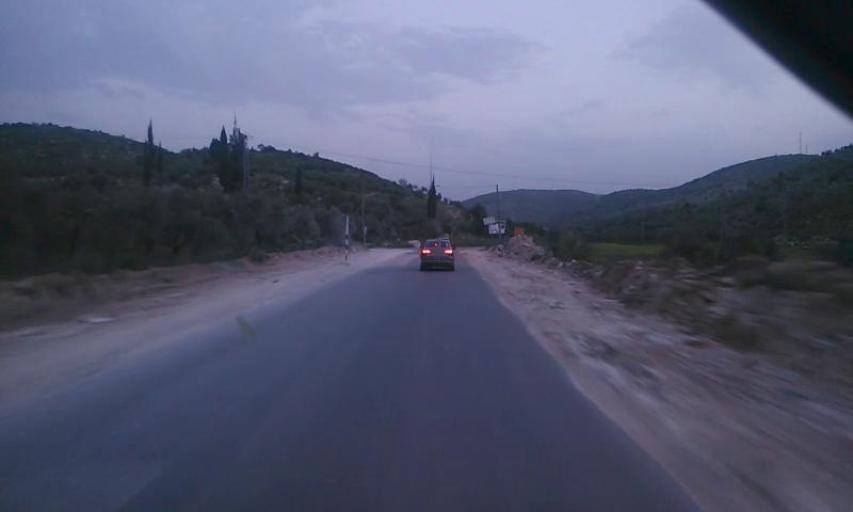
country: PS
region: West Bank
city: Ramin
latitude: 32.2956
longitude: 35.1328
